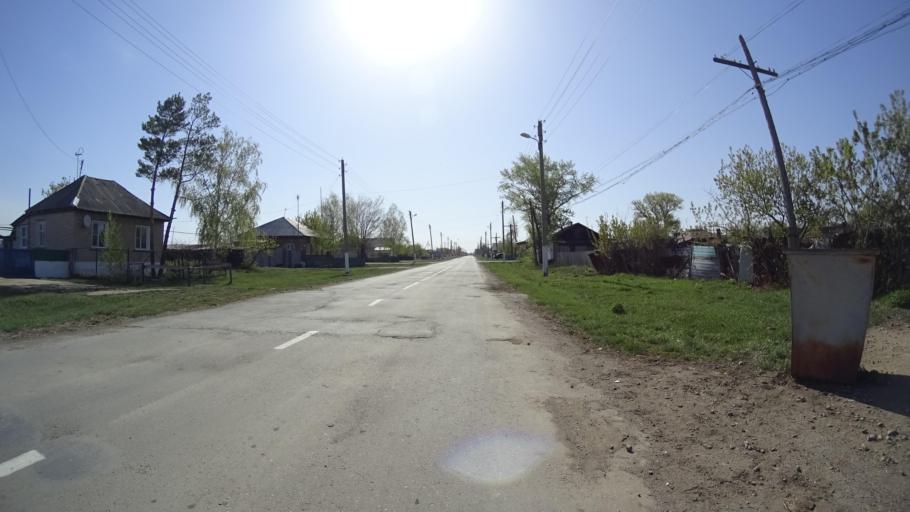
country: RU
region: Chelyabinsk
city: Chesma
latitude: 53.8000
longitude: 61.0228
